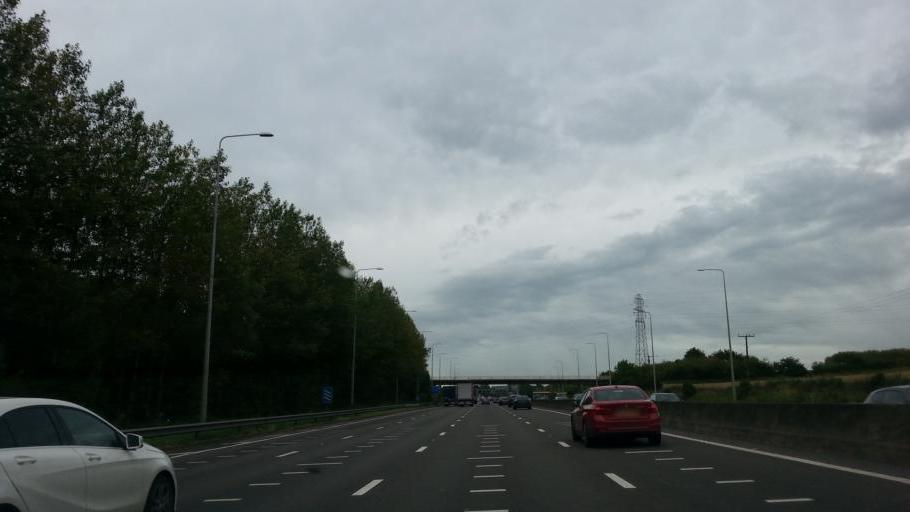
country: GB
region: England
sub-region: Kirklees
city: Cleckheaton
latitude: 53.7054
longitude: -1.7433
